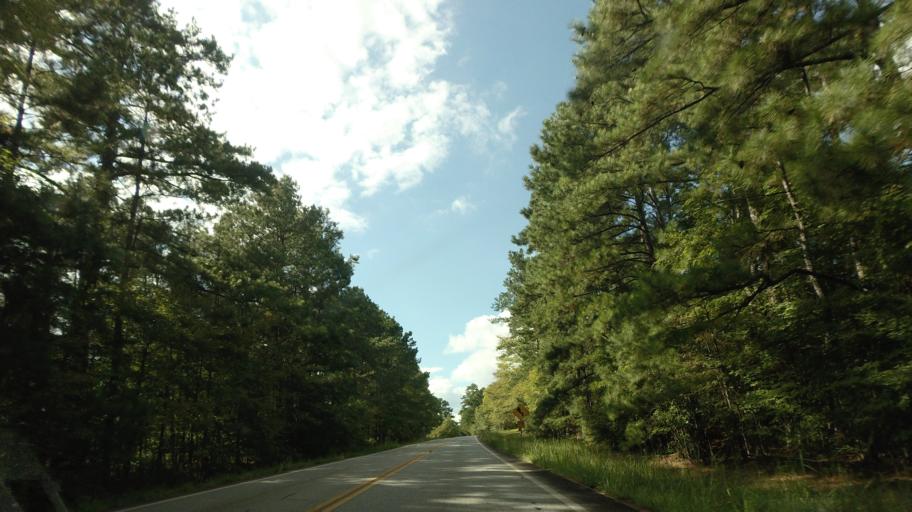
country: US
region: Georgia
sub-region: Monroe County
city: Forsyth
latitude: 33.0232
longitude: -83.7625
